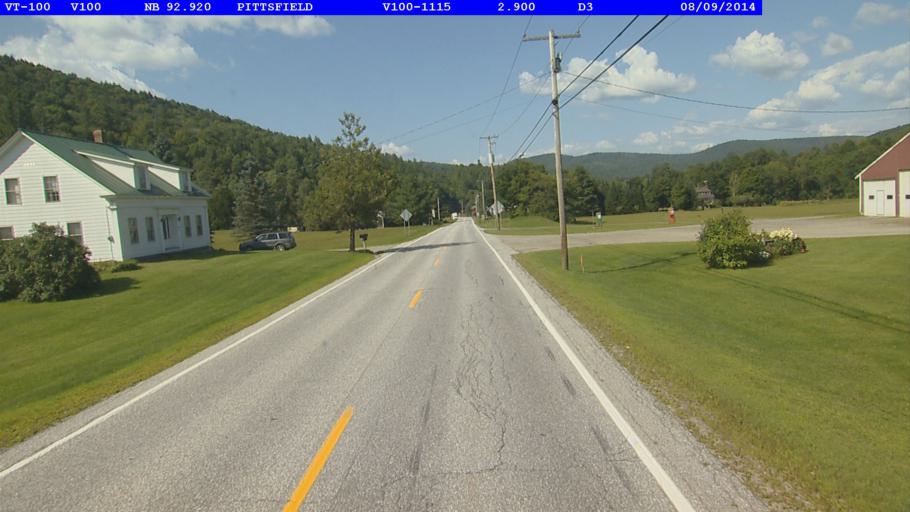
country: US
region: Vermont
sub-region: Rutland County
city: Rutland
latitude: 43.7585
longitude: -72.8196
